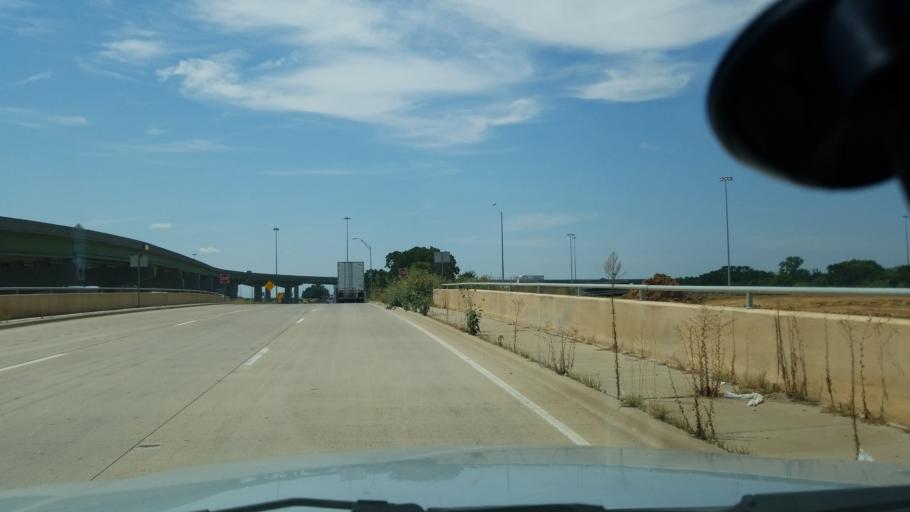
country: US
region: Texas
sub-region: Dallas County
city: Irving
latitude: 32.8414
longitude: -96.9153
